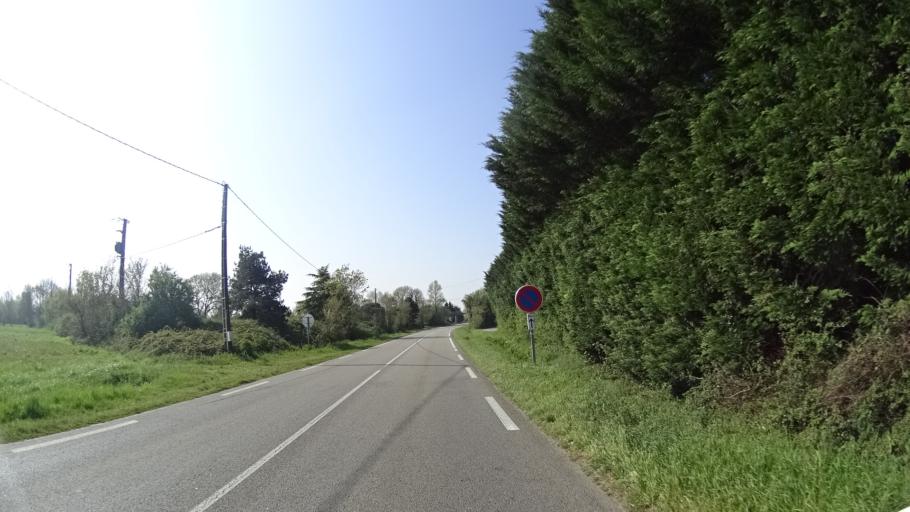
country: FR
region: Pays de la Loire
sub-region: Departement de la Loire-Atlantique
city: Port-Saint-Pere
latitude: 47.1226
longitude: -1.7643
